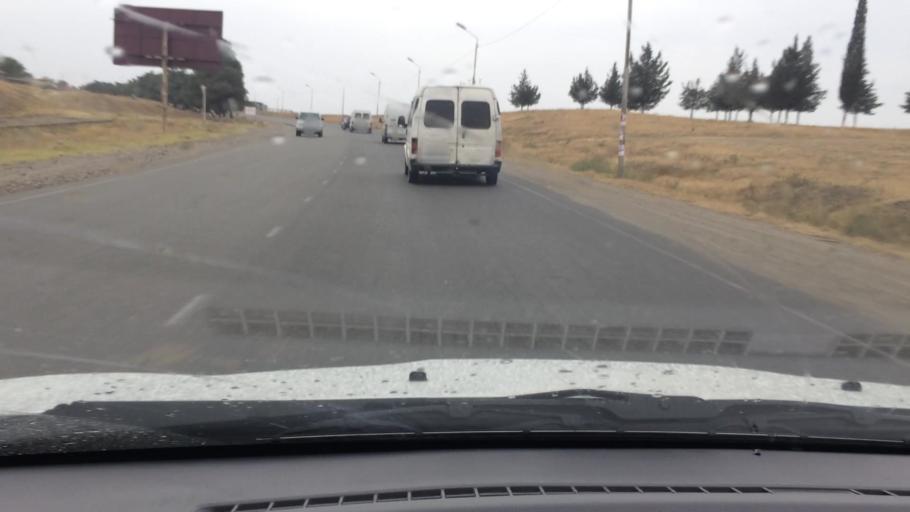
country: GE
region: Kvemo Kartli
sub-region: Marneuli
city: Marneuli
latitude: 41.5022
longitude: 44.8026
